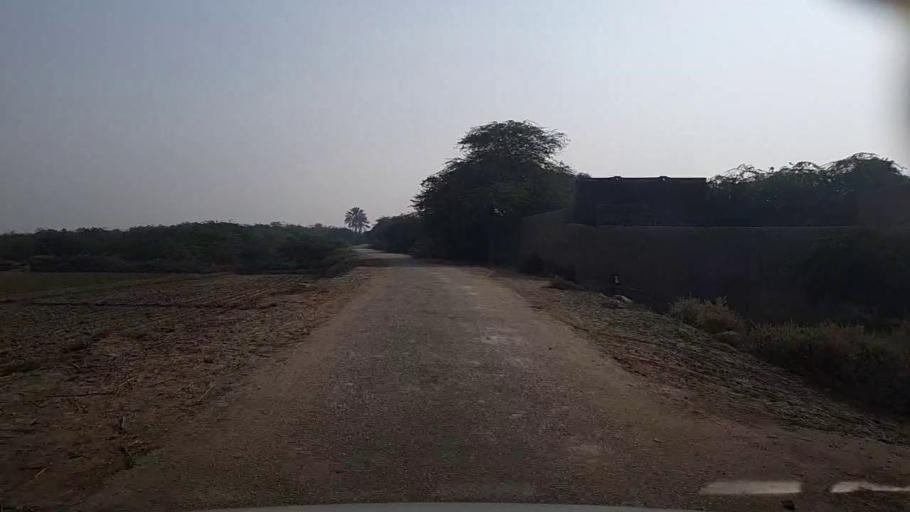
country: PK
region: Sindh
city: Kandiari
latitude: 27.0501
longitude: 68.4617
